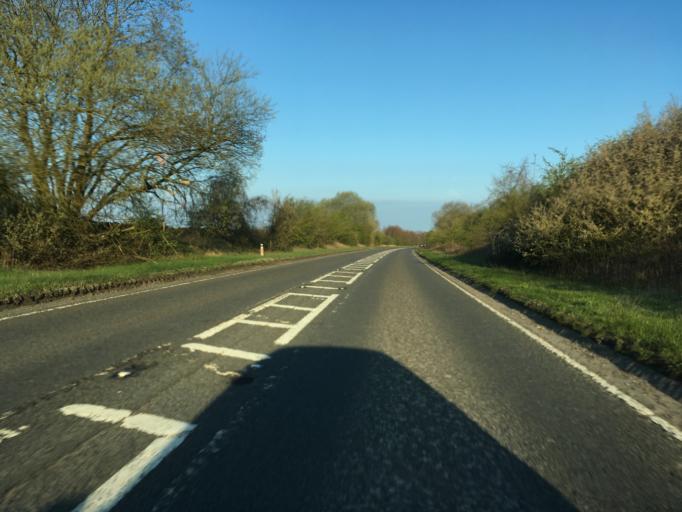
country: GB
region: England
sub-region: Gloucestershire
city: Westfield
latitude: 51.8459
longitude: -1.8737
